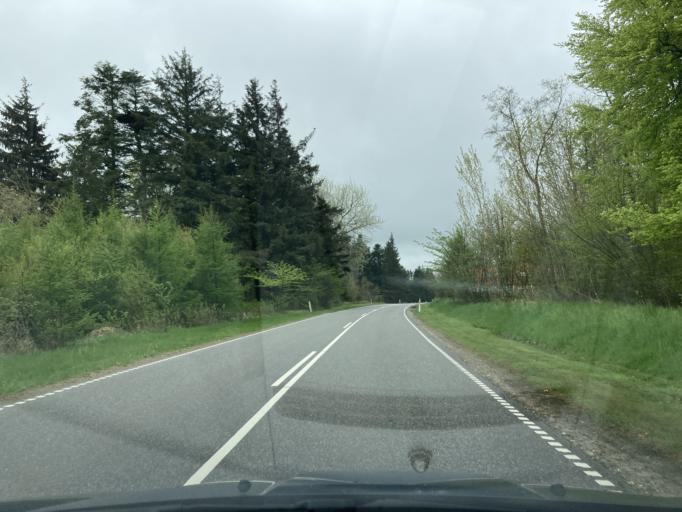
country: DK
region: North Denmark
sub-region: Thisted Kommune
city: Hurup
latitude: 56.8736
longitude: 8.3858
